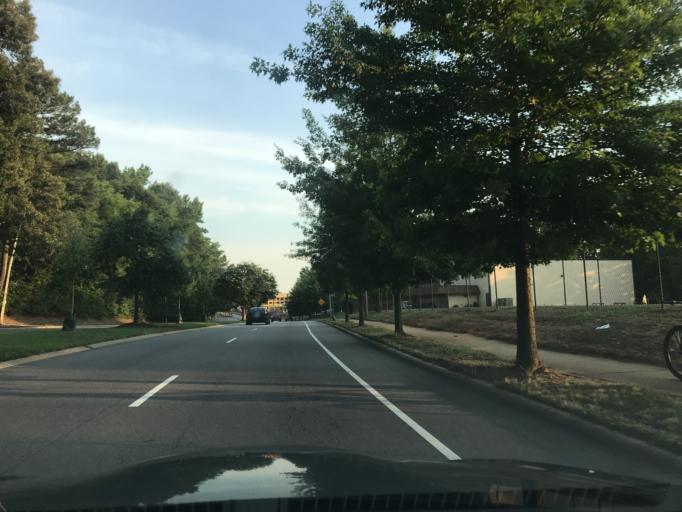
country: US
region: North Carolina
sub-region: Wake County
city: Raleigh
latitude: 35.7901
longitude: -78.6132
